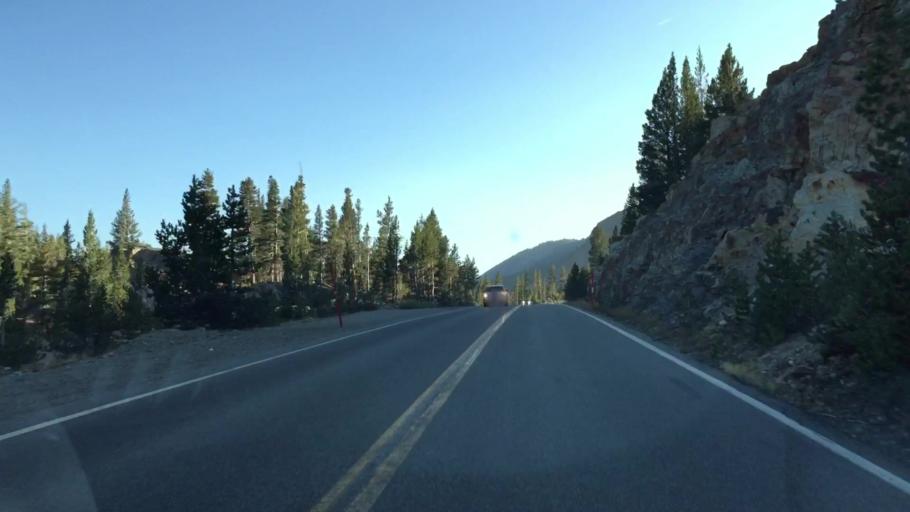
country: US
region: California
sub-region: Mono County
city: Bridgeport
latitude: 37.9331
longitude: -119.2493
